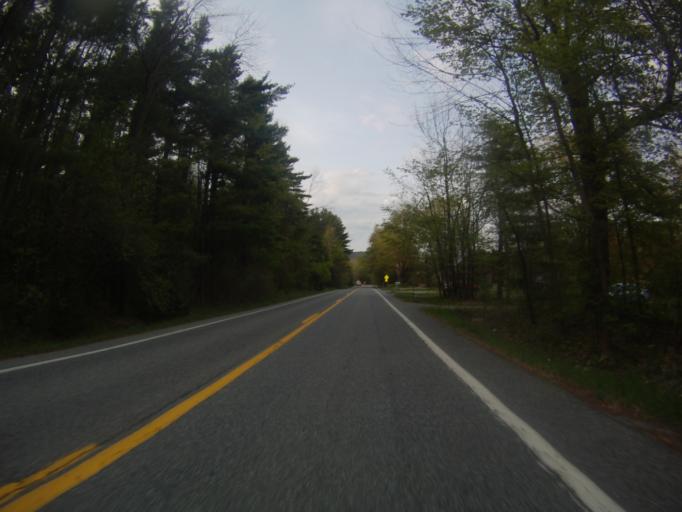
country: US
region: New York
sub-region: Essex County
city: Ticonderoga
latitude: 43.7528
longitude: -73.5616
